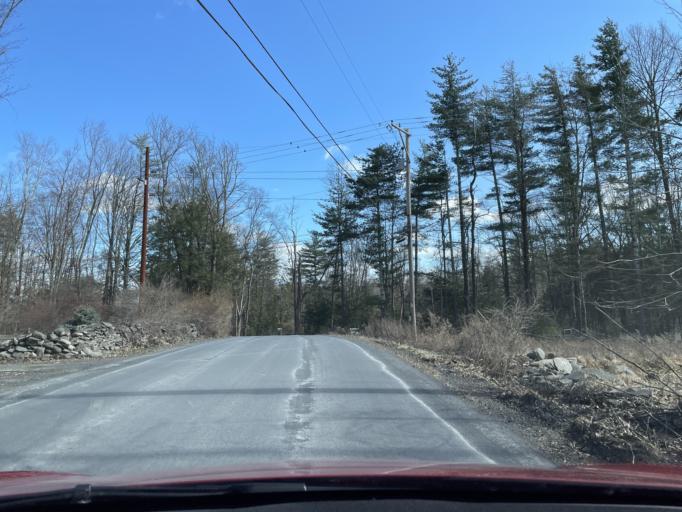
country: US
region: New York
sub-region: Ulster County
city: Woodstock
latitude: 42.0309
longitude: -74.0992
